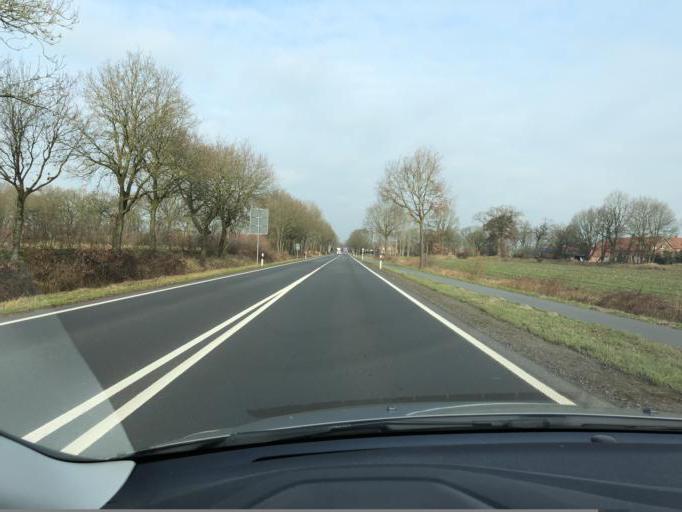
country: DE
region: Lower Saxony
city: Hesel
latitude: 53.3461
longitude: 7.6048
